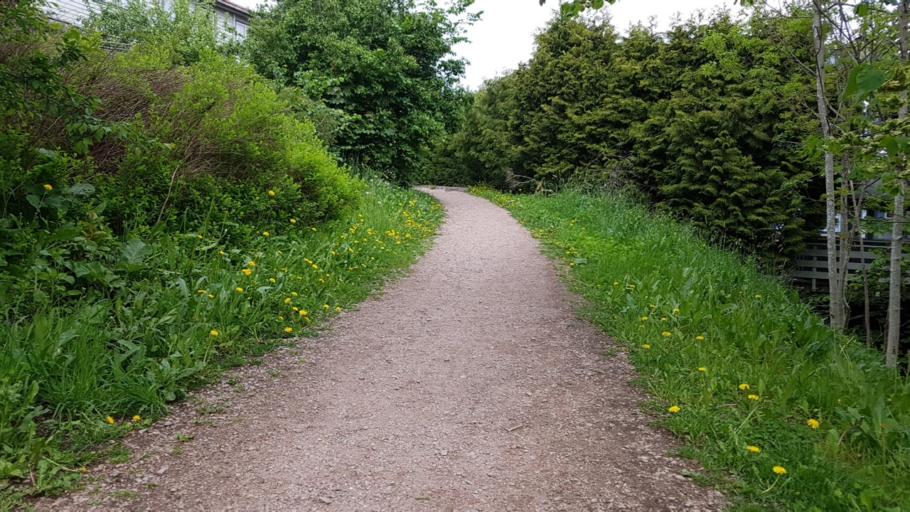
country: NO
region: Oslo
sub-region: Oslo
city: Oslo
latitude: 59.9409
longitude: 10.8227
